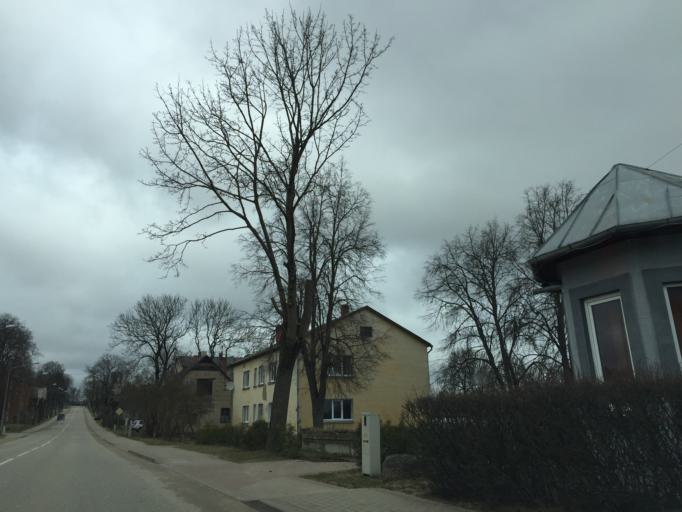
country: LV
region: Ilukste
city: Ilukste
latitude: 55.9798
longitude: 26.2940
